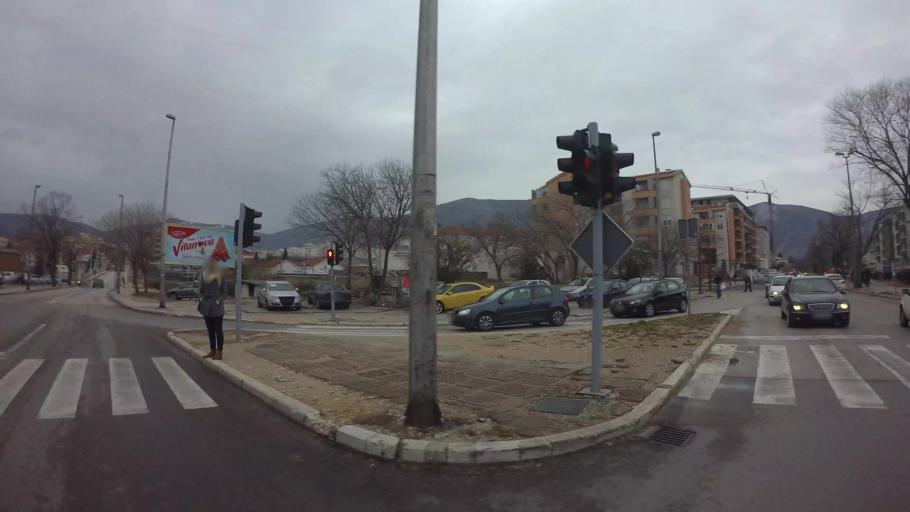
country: BA
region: Federation of Bosnia and Herzegovina
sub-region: Hercegovacko-Bosanski Kanton
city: Mostar
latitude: 43.3485
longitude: 17.8127
